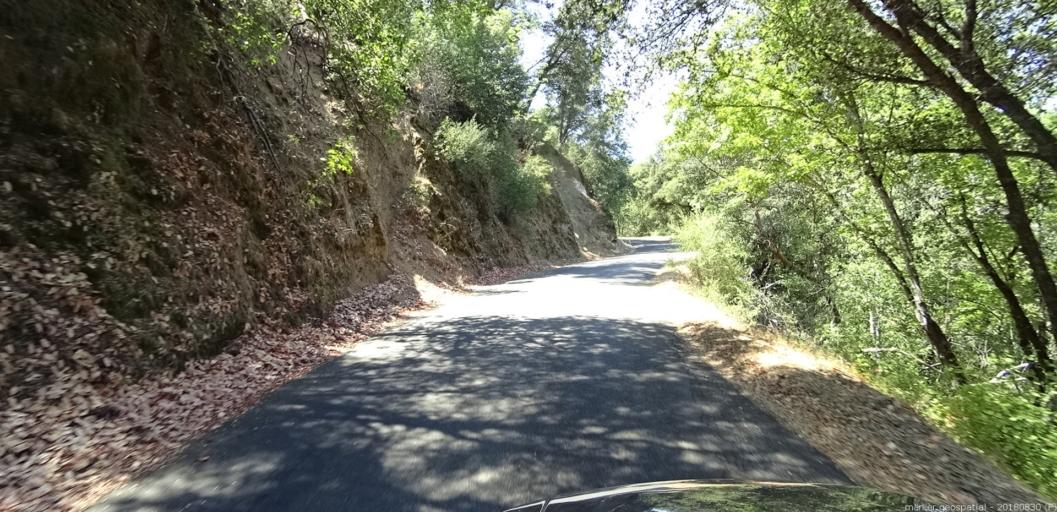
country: US
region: California
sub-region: Monterey County
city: Greenfield
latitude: 36.0155
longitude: -121.4303
